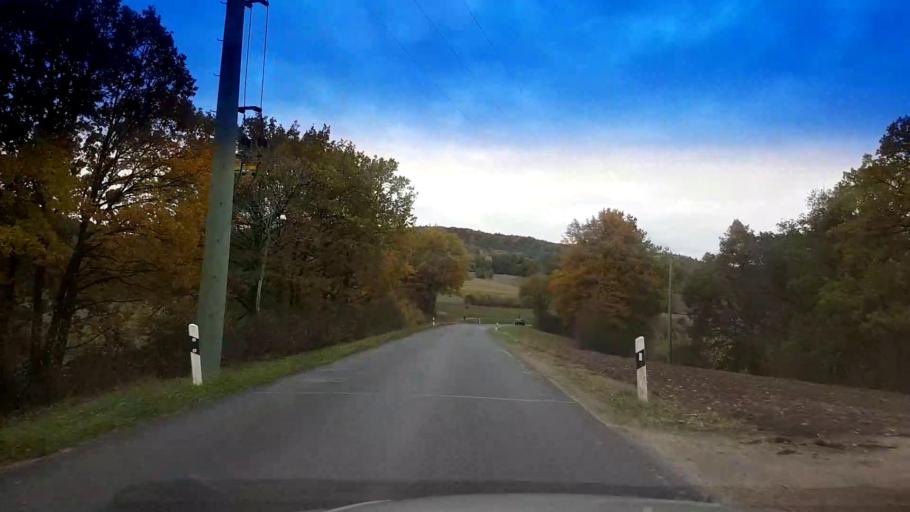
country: DE
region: Bavaria
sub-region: Upper Franconia
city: Viereth-Trunstadt
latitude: 49.9167
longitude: 10.7658
